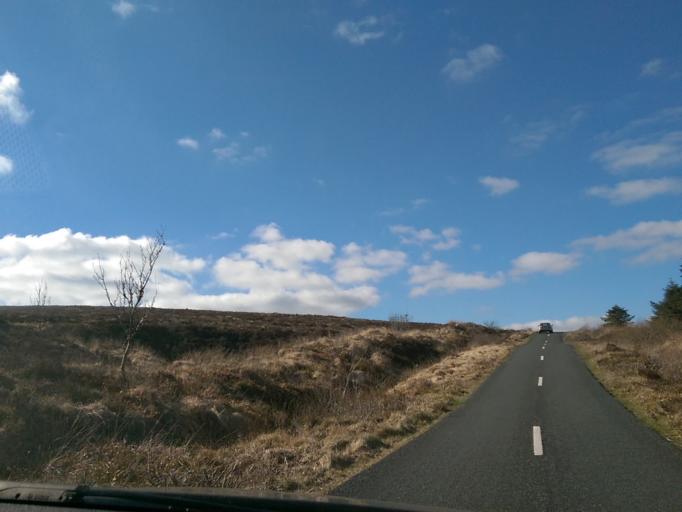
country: IE
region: Leinster
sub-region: Laois
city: Mountrath
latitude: 53.0765
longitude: -7.5918
